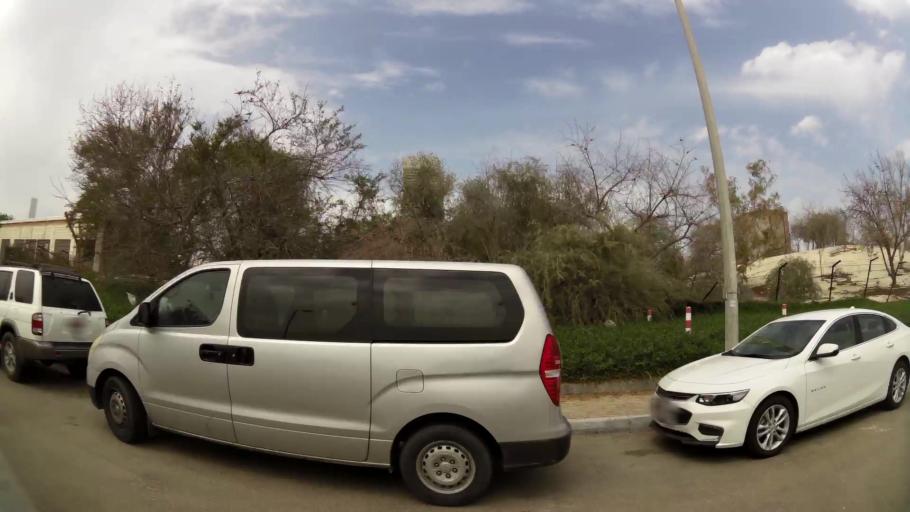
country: AE
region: Abu Dhabi
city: Abu Dhabi
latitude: 24.4653
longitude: 54.3437
